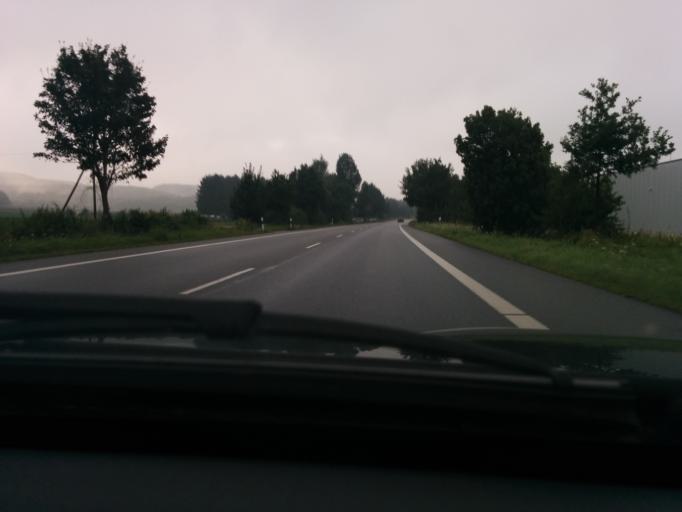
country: DE
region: North Rhine-Westphalia
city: Halle
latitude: 52.0482
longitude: 8.3813
